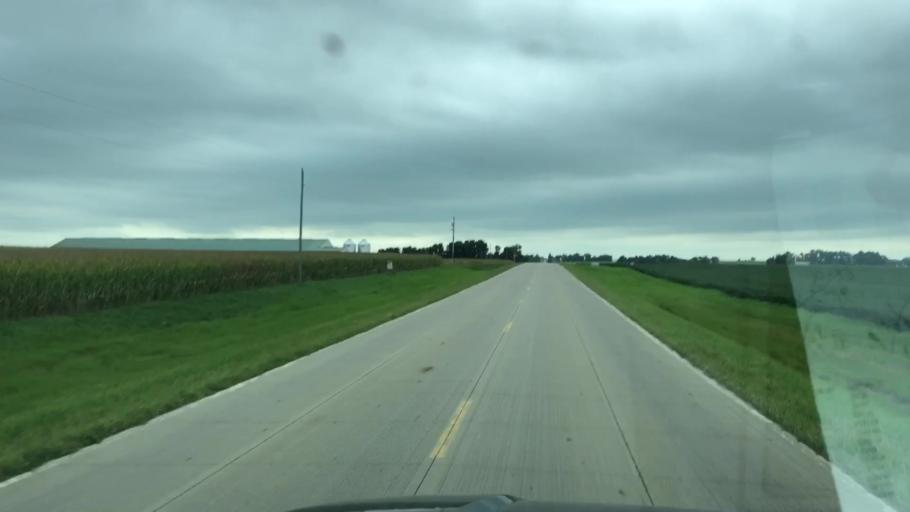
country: US
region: Iowa
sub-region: O'Brien County
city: Sheldon
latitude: 43.1256
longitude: -95.9790
